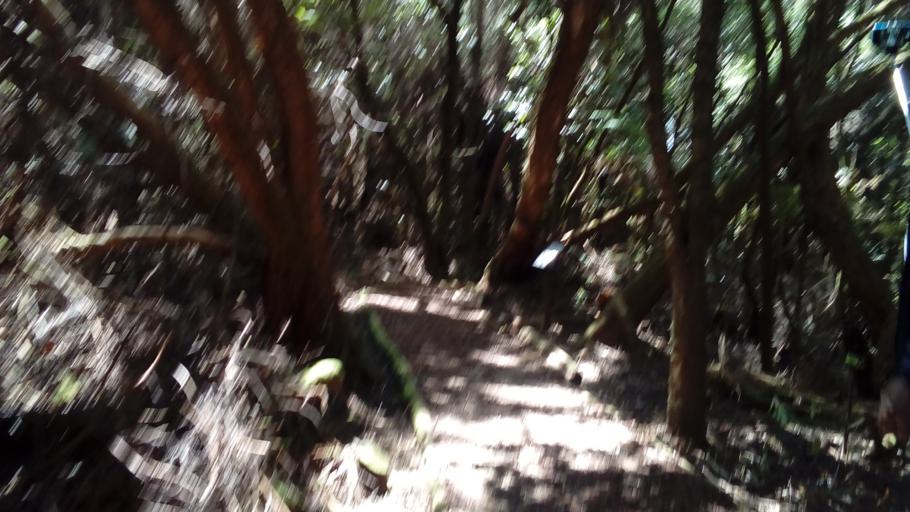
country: CR
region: Alajuela
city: Rio Segundo
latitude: 10.1854
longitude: -84.2348
